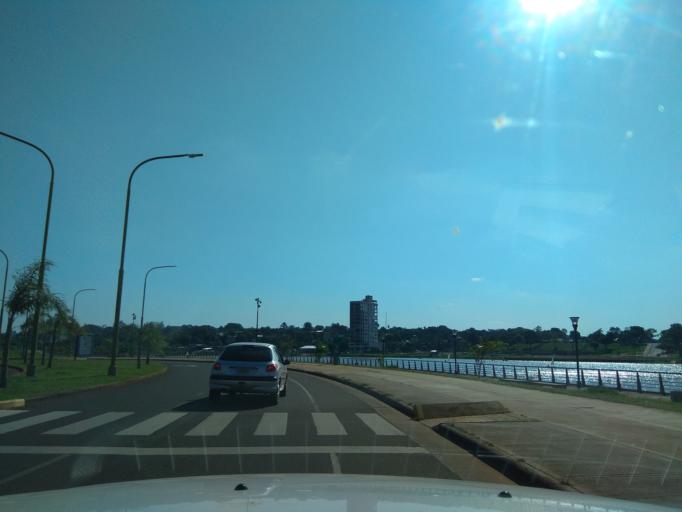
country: AR
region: Misiones
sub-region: Departamento de Capital
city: Posadas
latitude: -27.3563
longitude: -55.9074
